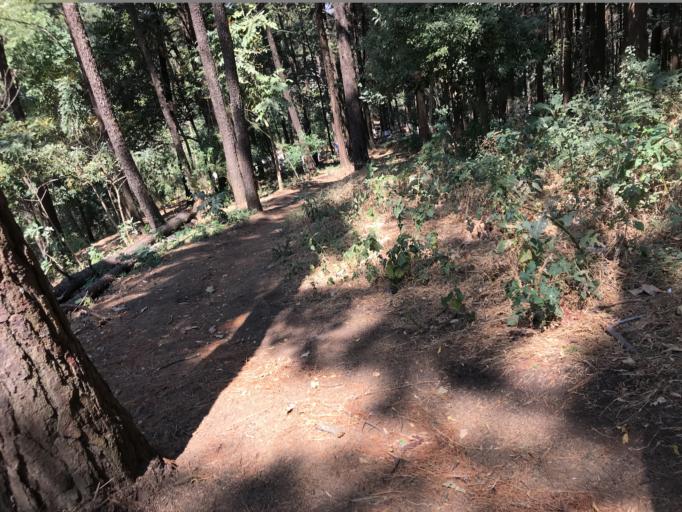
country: GT
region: Guatemala
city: Petapa
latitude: 14.4824
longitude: -90.5567
